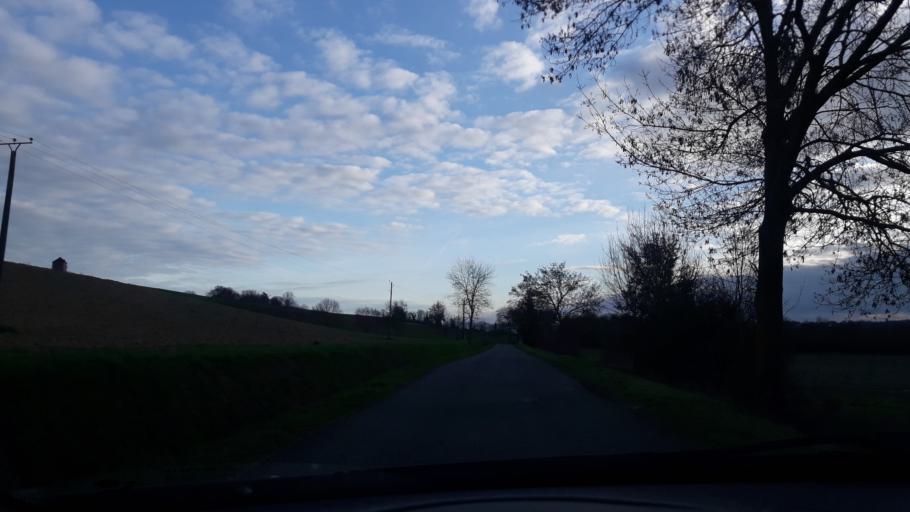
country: FR
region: Midi-Pyrenees
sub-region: Departement de la Haute-Garonne
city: Levignac
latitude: 43.6580
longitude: 1.1578
